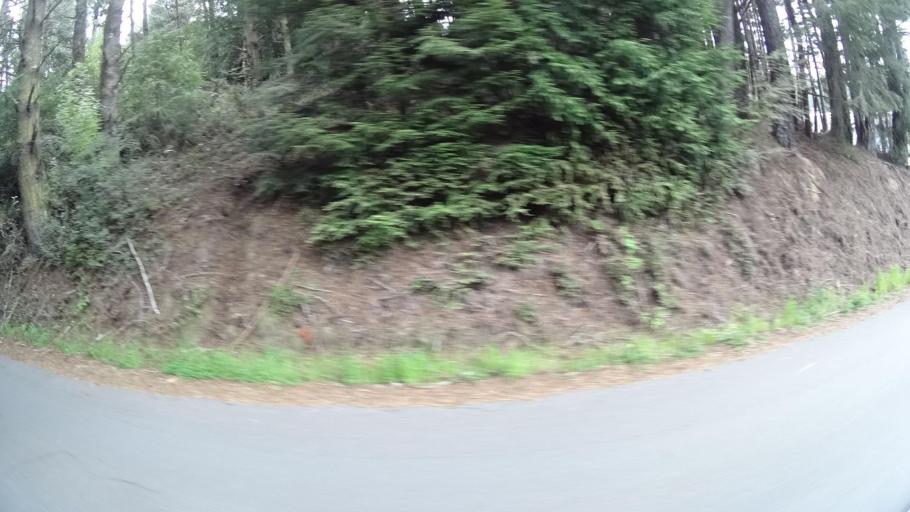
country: US
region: California
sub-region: Humboldt County
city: Bayside
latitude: 40.8474
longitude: -124.0486
